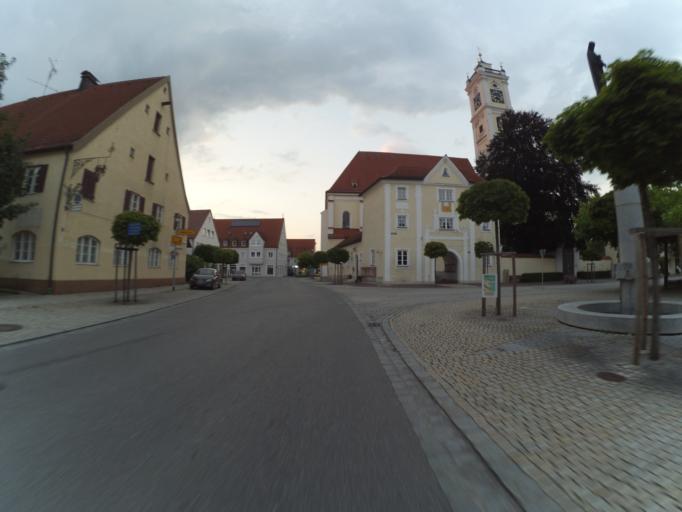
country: DE
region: Bavaria
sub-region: Swabia
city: Turkheim
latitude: 48.0625
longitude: 10.6402
